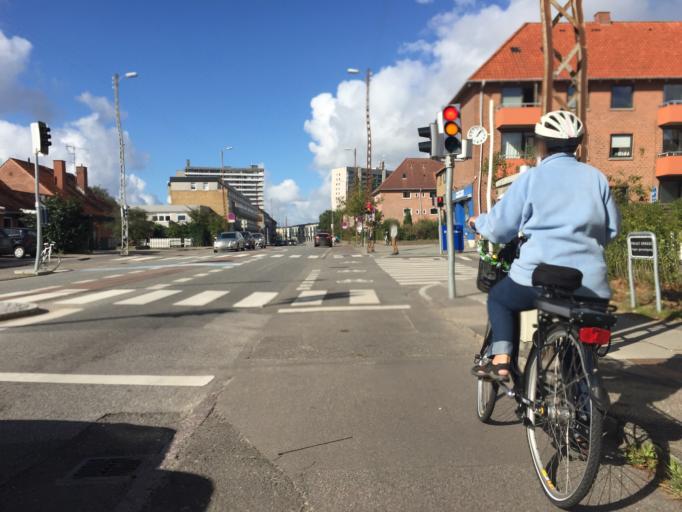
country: DK
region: Capital Region
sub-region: Gladsaxe Municipality
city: Buddinge
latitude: 55.7581
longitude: 12.4600
